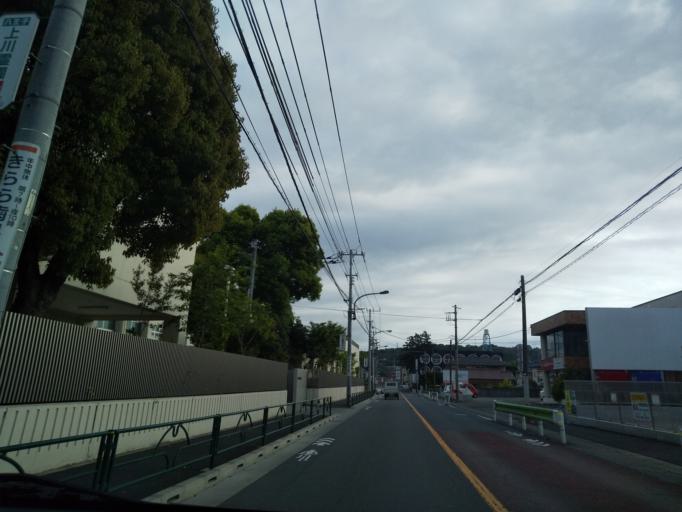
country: JP
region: Tokyo
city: Hachioji
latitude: 35.6853
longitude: 139.3041
